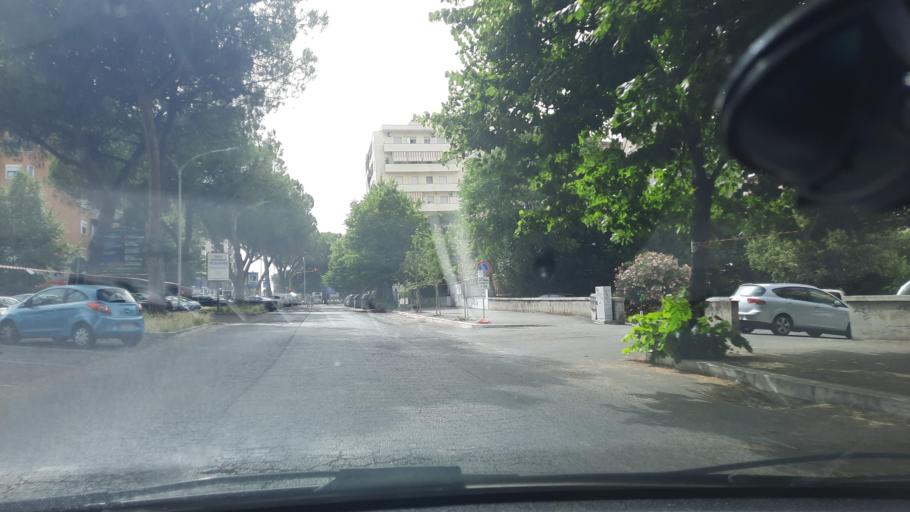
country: IT
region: Latium
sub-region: Citta metropolitana di Roma Capitale
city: Rome
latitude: 41.8563
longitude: 12.4826
